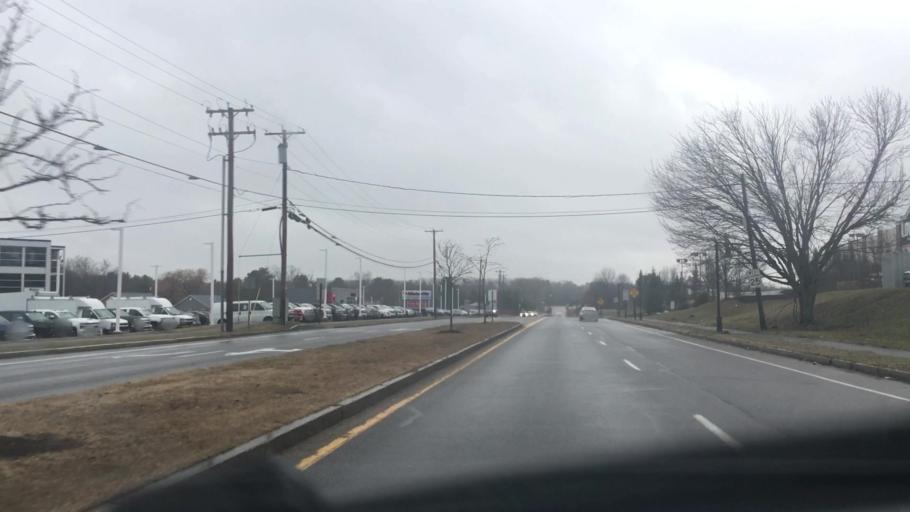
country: US
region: Maine
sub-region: Cumberland County
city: South Portland Gardens
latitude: 43.6740
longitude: -70.3213
